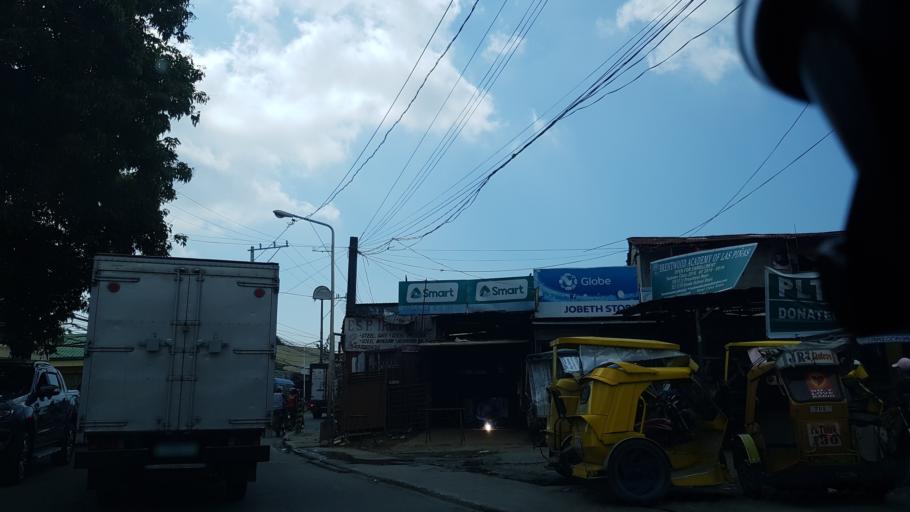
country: PH
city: Sambayanihan People's Village
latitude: 14.4612
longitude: 120.9938
